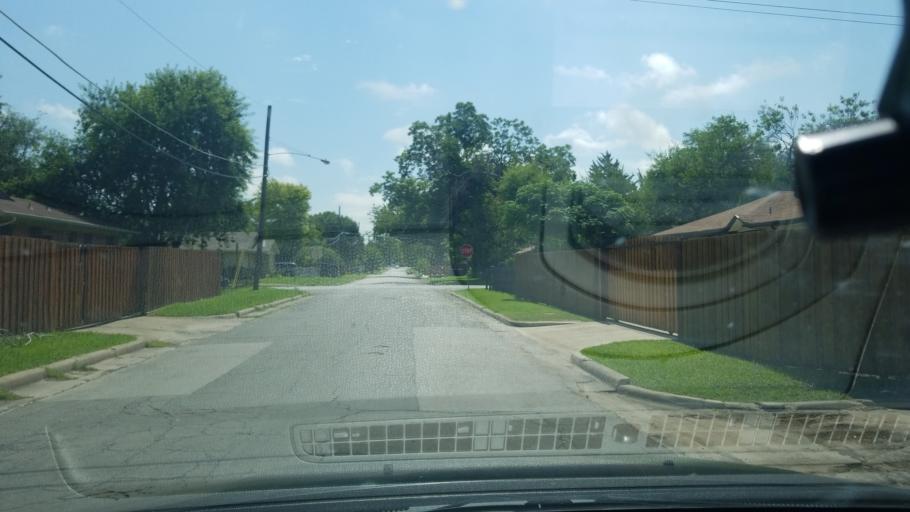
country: US
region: Texas
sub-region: Dallas County
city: Balch Springs
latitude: 32.7524
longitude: -96.6872
